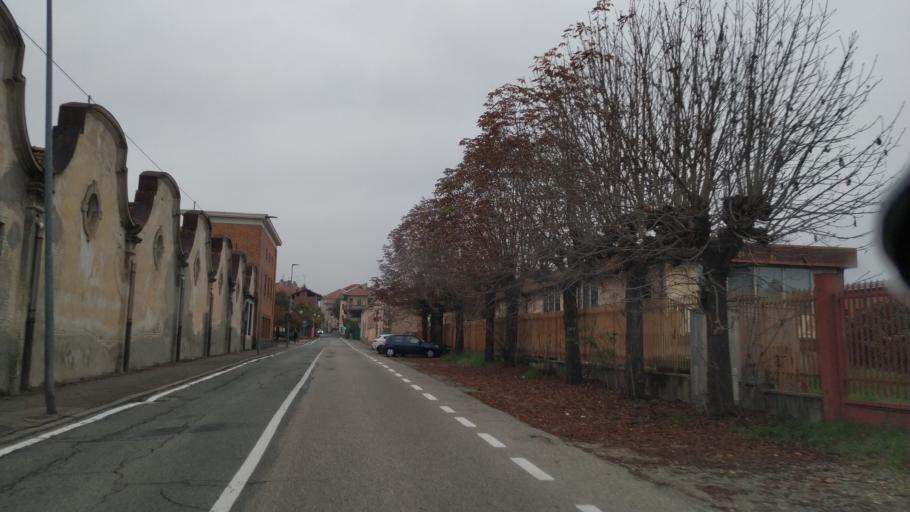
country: IT
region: Piedmont
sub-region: Provincia di Biella
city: Cossato
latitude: 45.5663
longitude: 8.1794
